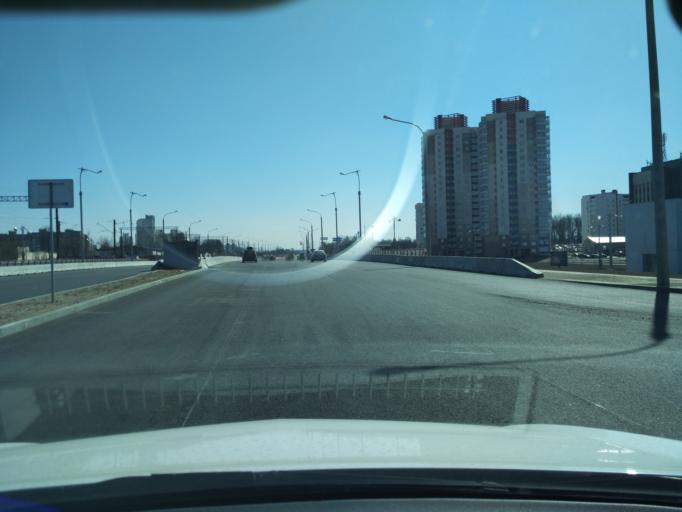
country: BY
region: Minsk
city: Minsk
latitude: 53.8728
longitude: 27.5614
